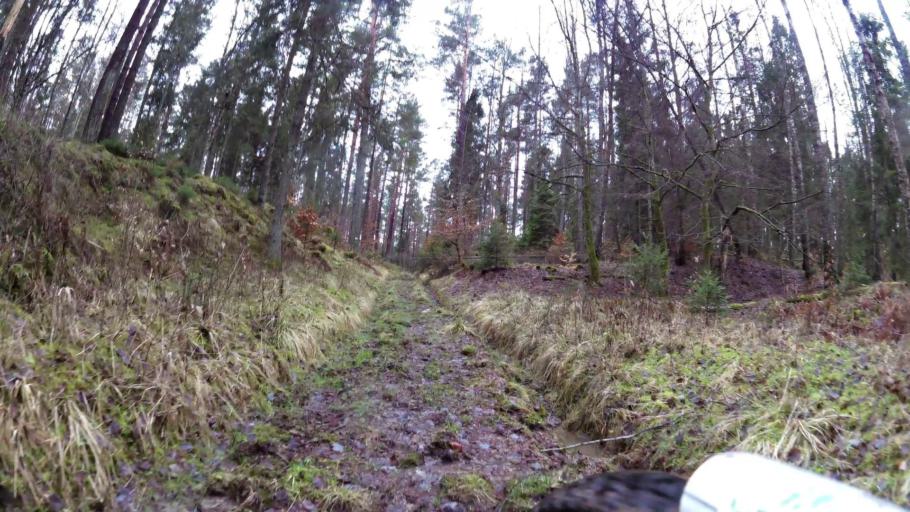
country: PL
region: Pomeranian Voivodeship
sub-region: Powiat bytowski
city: Kolczyglowy
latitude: 54.2435
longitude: 17.2764
